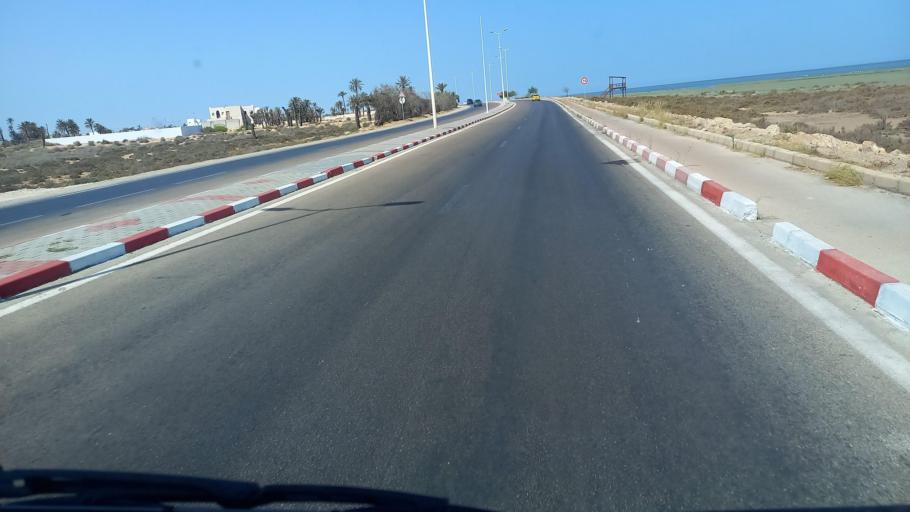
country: TN
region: Madanin
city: Houmt Souk
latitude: 33.8737
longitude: 10.9284
